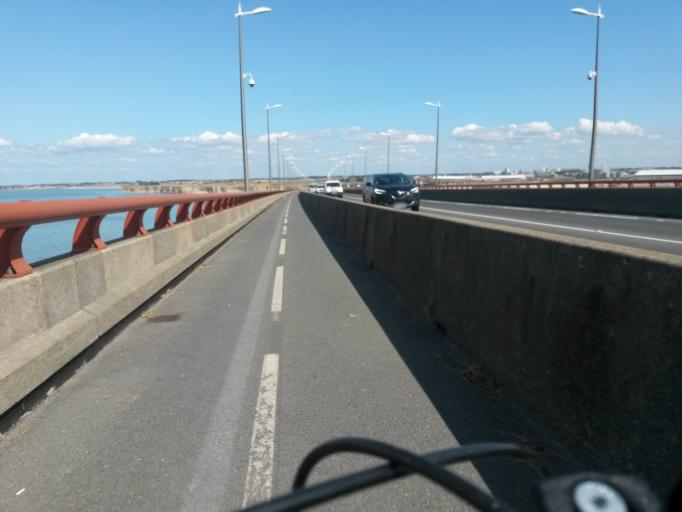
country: FR
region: Poitou-Charentes
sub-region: Departement de la Charente-Maritime
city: Rivedoux-Plage
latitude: 46.1737
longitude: -1.2334
